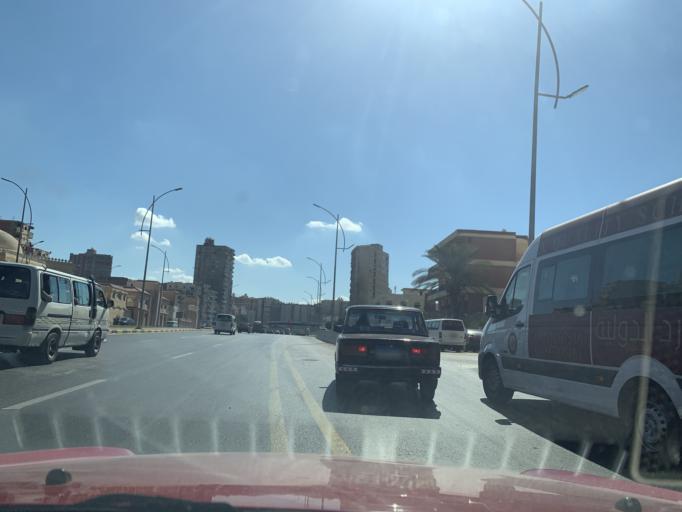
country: EG
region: Alexandria
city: Alexandria
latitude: 31.2164
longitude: 29.9629
